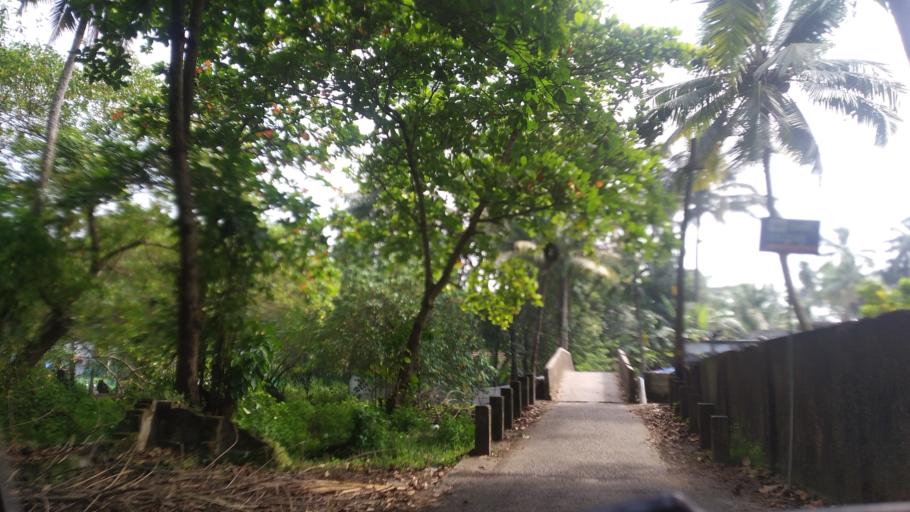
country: IN
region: Kerala
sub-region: Ernakulam
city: Elur
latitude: 10.0881
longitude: 76.2052
